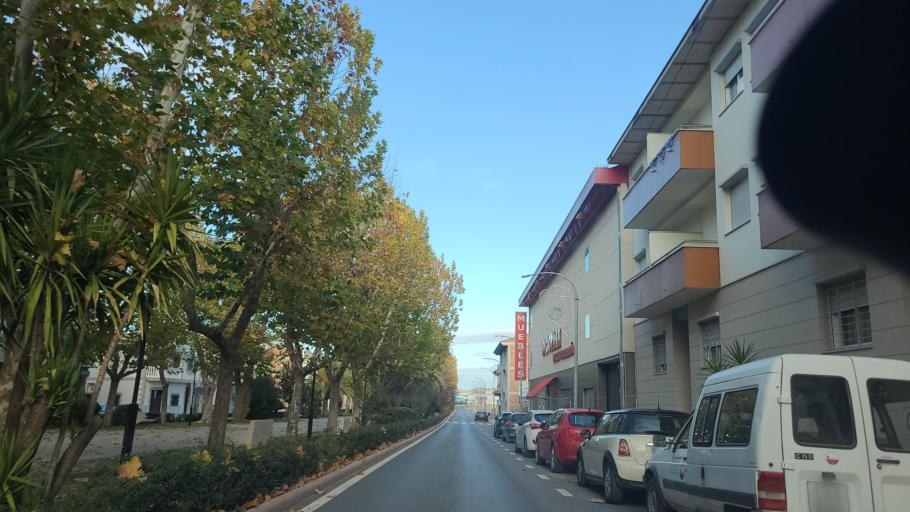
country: ES
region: Andalusia
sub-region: Provincia de Jaen
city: Mengibar
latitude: 37.9711
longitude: -3.8009
